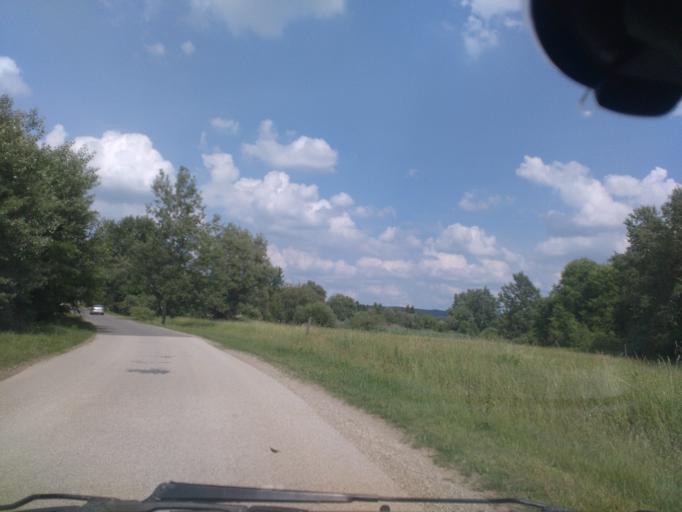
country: HU
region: Pest
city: Veresegyhaz
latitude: 47.6396
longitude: 19.2632
